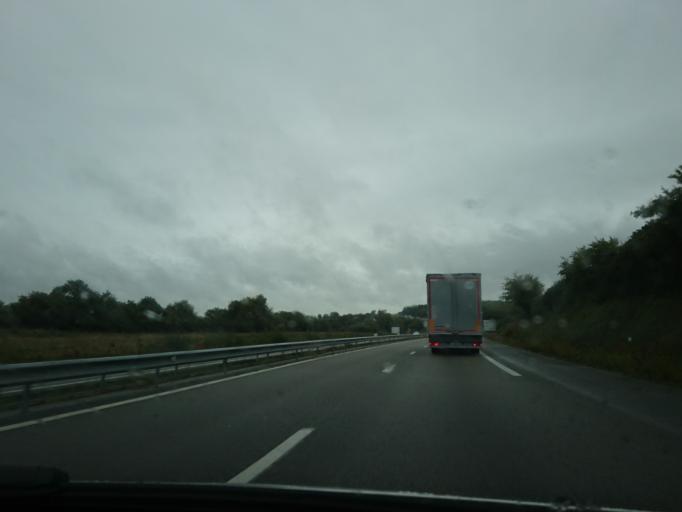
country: FR
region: Brittany
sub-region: Departement du Morbihan
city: Ambon
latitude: 47.5951
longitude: -2.5690
